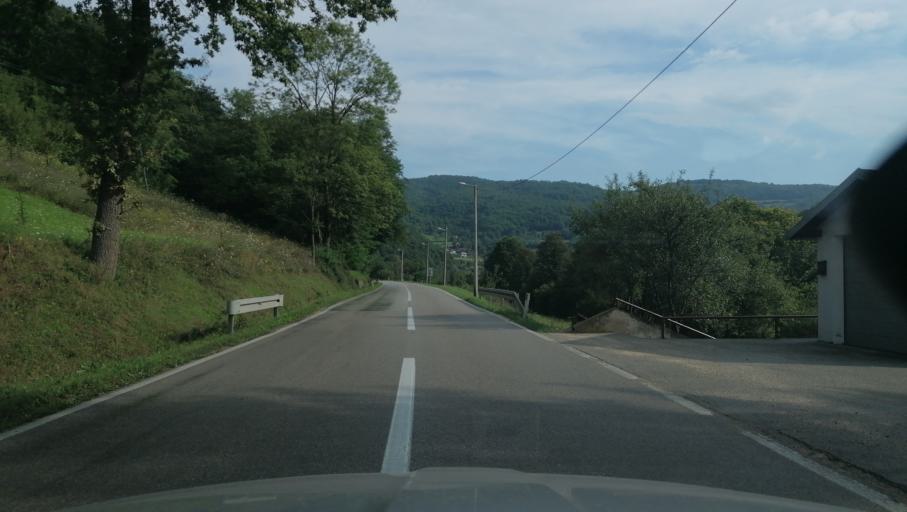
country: BA
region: Republika Srpska
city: Hiseti
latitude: 44.6686
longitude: 17.1454
